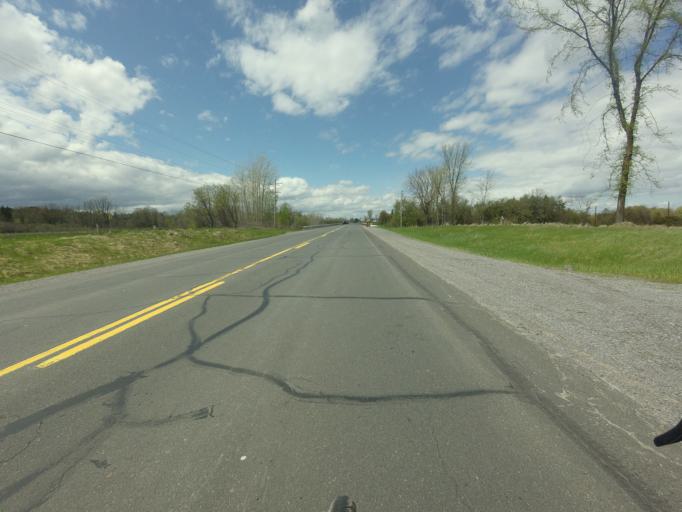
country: CA
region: Ontario
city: Carleton Place
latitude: 45.2574
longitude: -76.2521
